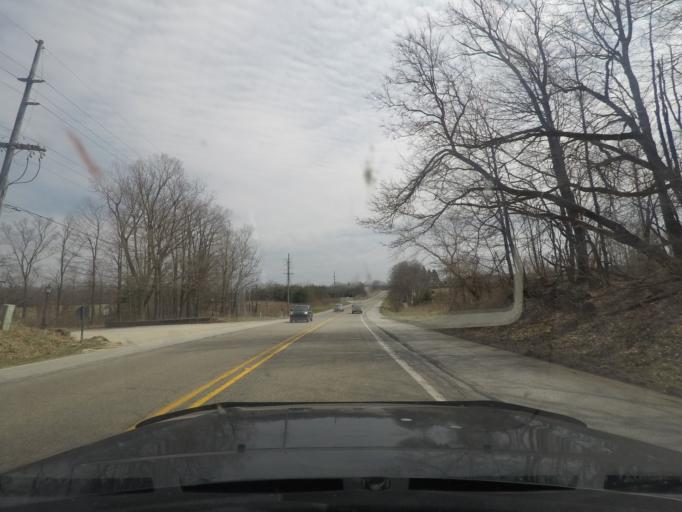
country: US
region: Indiana
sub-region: LaPorte County
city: LaPorte
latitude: 41.6502
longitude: -86.7575
